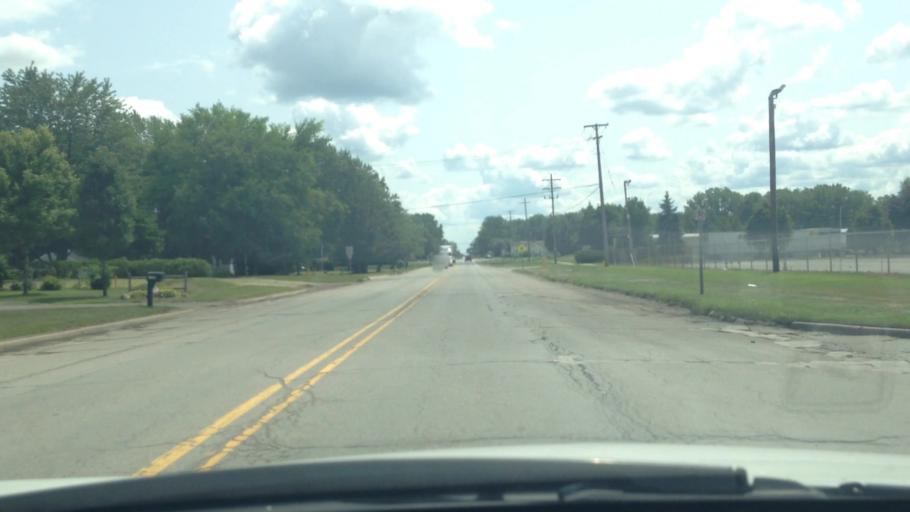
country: US
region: Michigan
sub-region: Wayne County
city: Inkster
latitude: 42.2643
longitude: -83.3089
